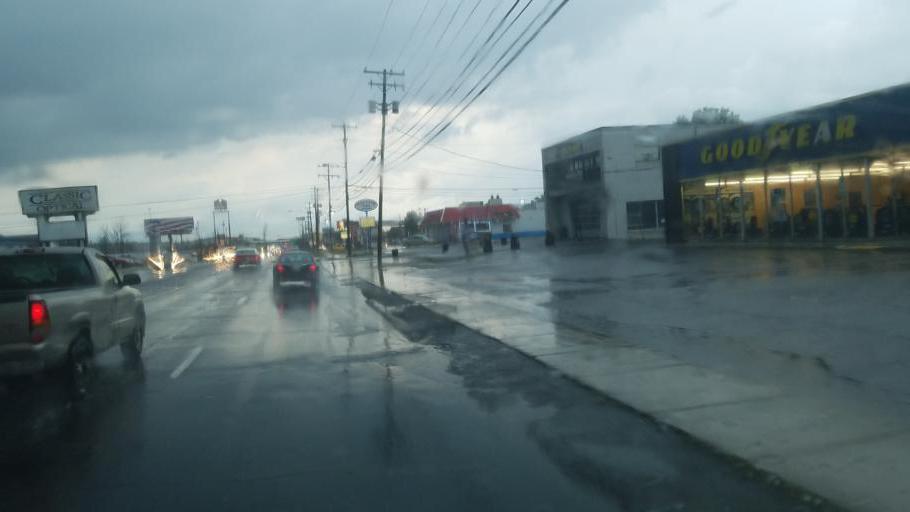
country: US
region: Ohio
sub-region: Trumbull County
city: Churchill
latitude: 41.1492
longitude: -80.6651
